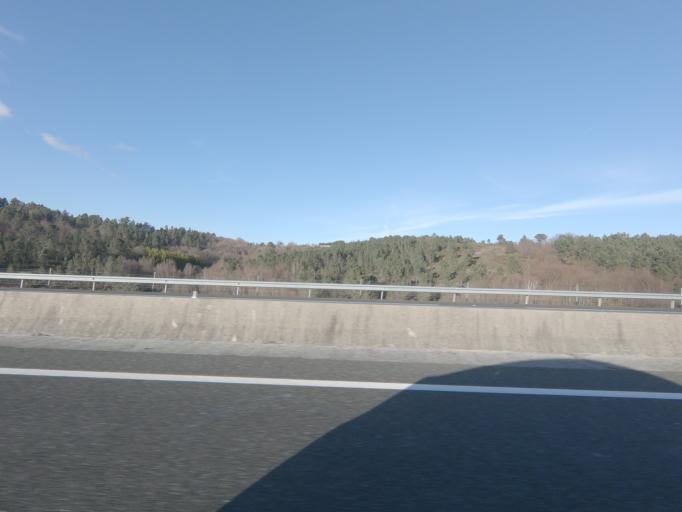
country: ES
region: Galicia
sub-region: Provincia de Pontevedra
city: Lalin
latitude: 42.6007
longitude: -8.0938
